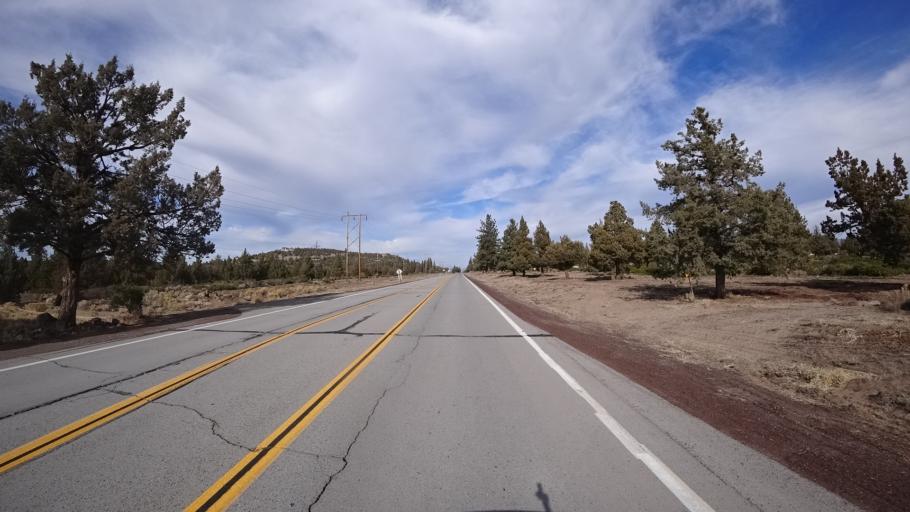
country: US
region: California
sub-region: Siskiyou County
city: Weed
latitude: 41.5289
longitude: -122.3647
